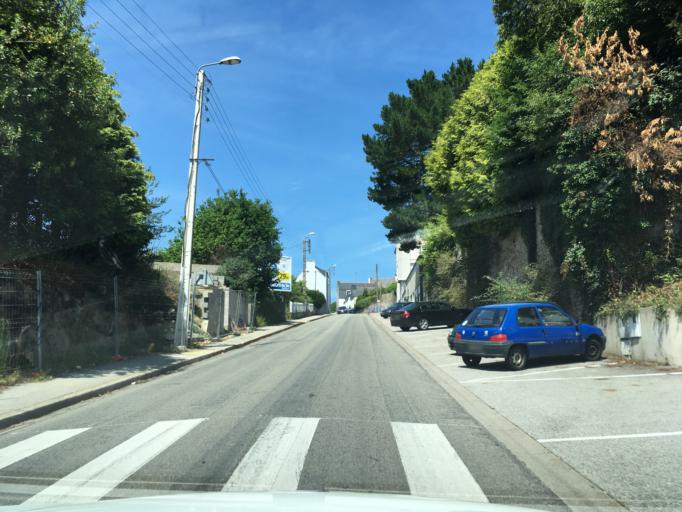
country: FR
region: Brittany
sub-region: Departement du Finistere
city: Quimper
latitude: 47.9927
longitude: -4.1191
